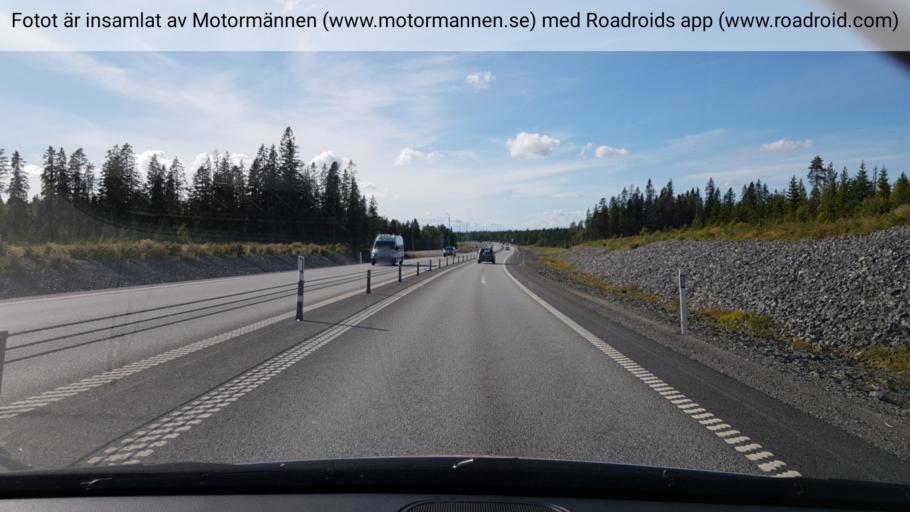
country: SE
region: Vaesterbotten
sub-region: Umea Kommun
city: Umea
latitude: 63.8551
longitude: 20.2644
